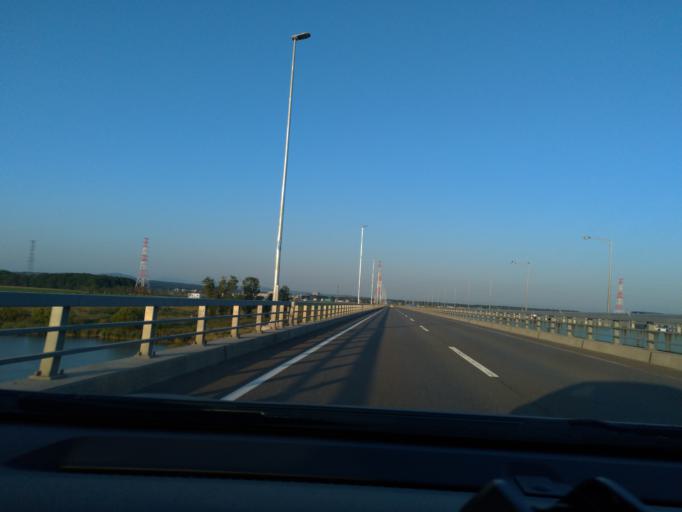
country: JP
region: Hokkaido
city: Ishikari
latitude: 43.1735
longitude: 141.4209
